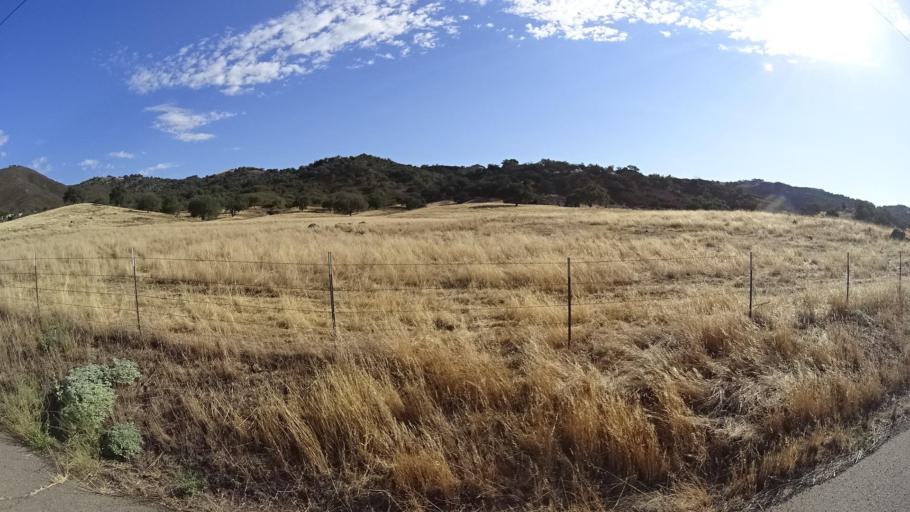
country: US
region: California
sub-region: San Diego County
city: Julian
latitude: 33.1445
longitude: -116.6880
